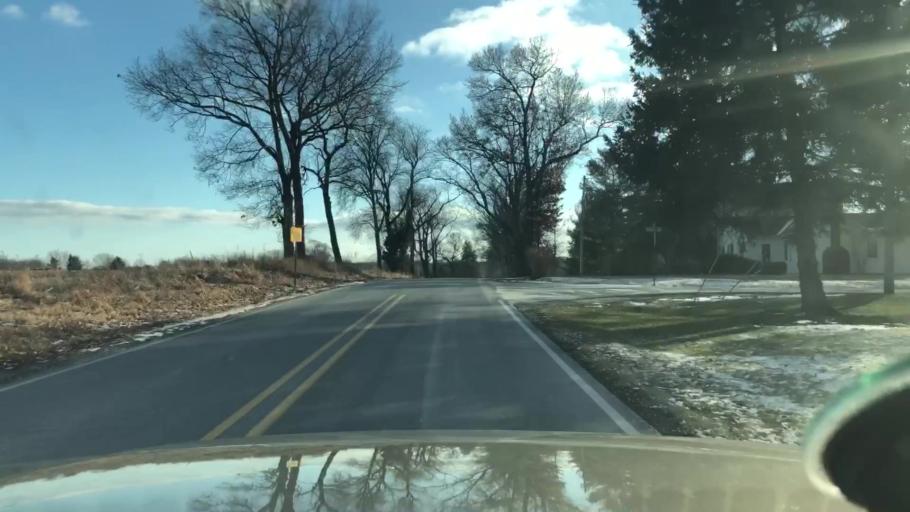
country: US
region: Michigan
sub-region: Jackson County
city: Vandercook Lake
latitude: 42.1677
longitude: -84.4521
